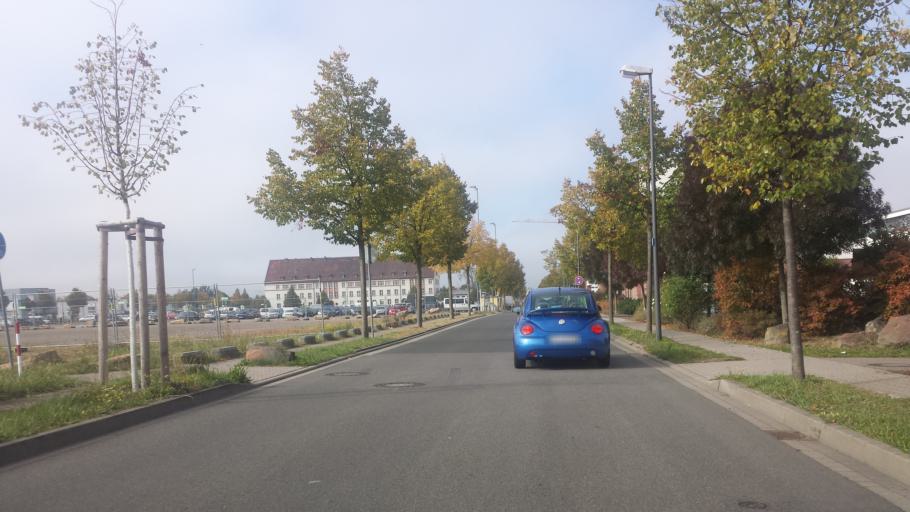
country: DE
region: Rheinland-Pfalz
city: Landau in der Pfalz
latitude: 49.1922
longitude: 8.1363
